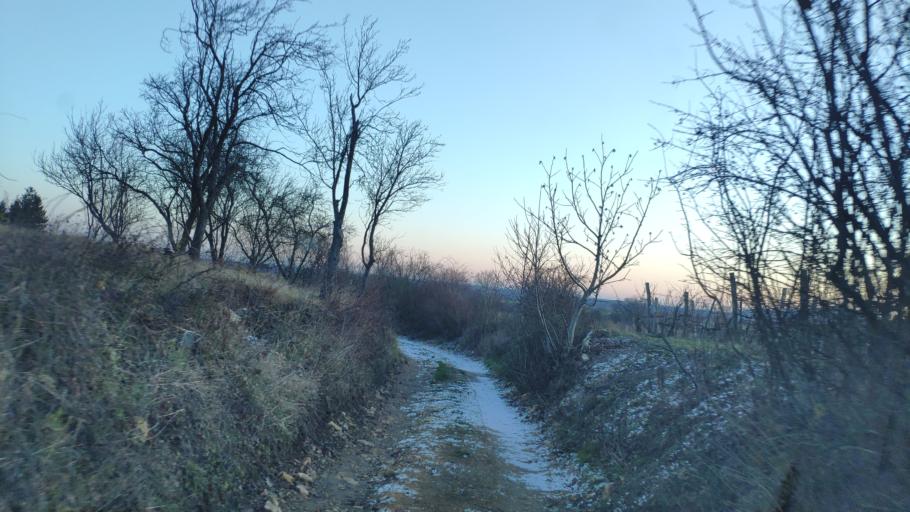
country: HU
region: Borsod-Abauj-Zemplen
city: Olaszliszka
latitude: 48.2741
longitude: 21.3974
